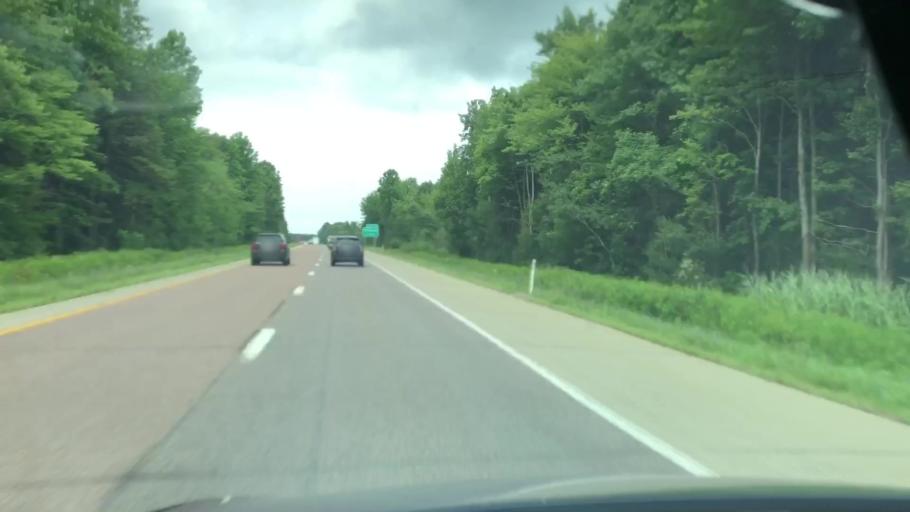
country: US
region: Pennsylvania
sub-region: Erie County
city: Edinboro
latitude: 41.9671
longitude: -80.1744
